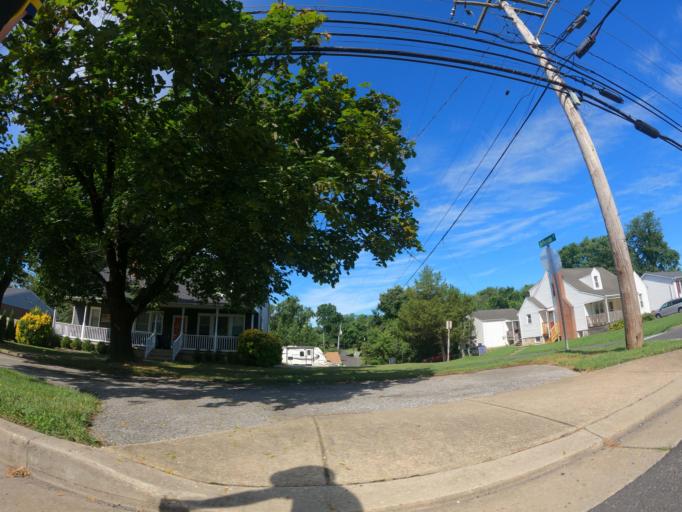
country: US
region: Maryland
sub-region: Howard County
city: Savage
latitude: 39.1427
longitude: -76.8254
